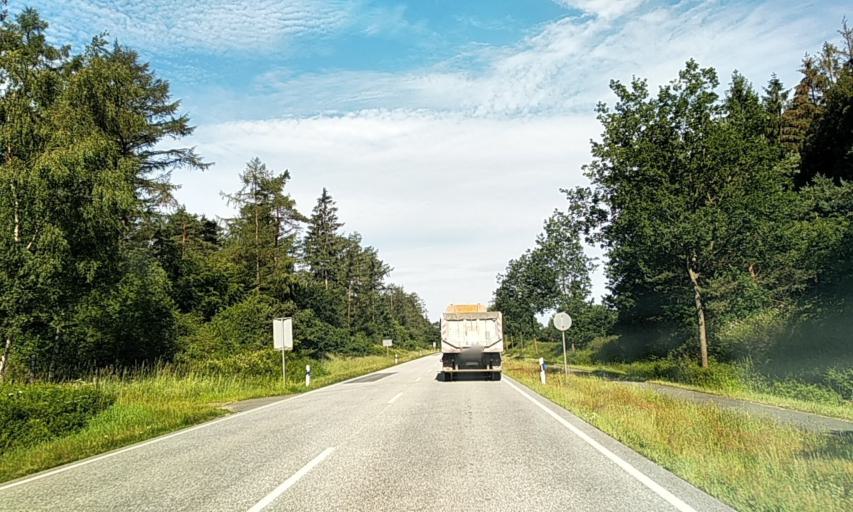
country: DE
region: Schleswig-Holstein
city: Lohe-Fohrden
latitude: 54.3502
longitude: 9.5716
